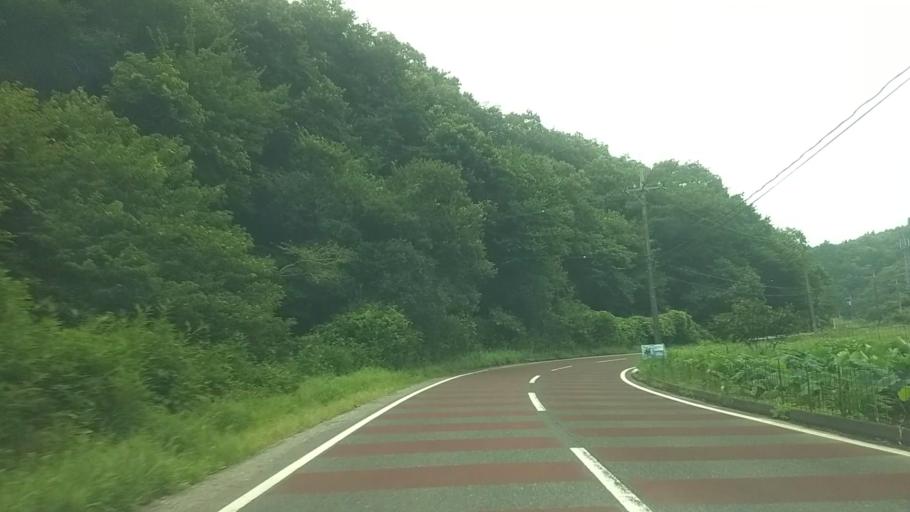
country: JP
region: Chiba
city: Kawaguchi
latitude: 35.2384
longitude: 140.0337
